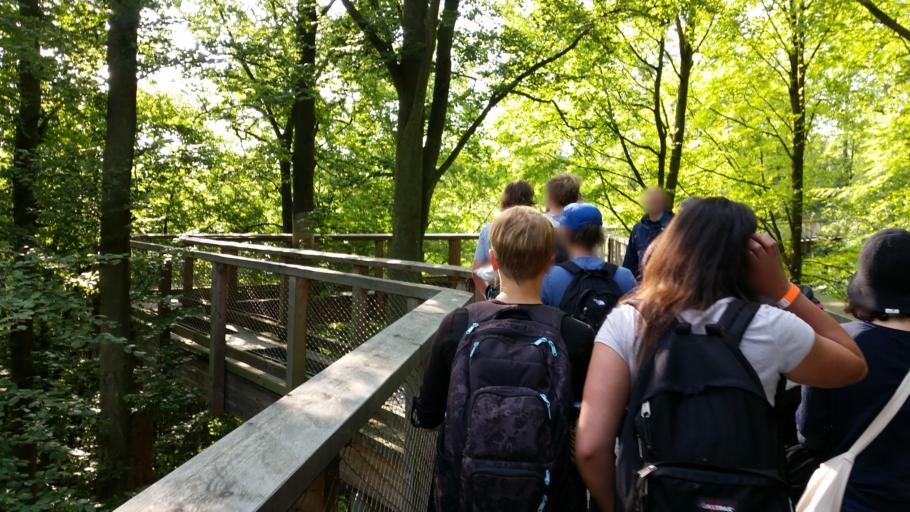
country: DE
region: Mecklenburg-Vorpommern
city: Ostseebad Binz
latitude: 54.4329
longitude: 13.5597
